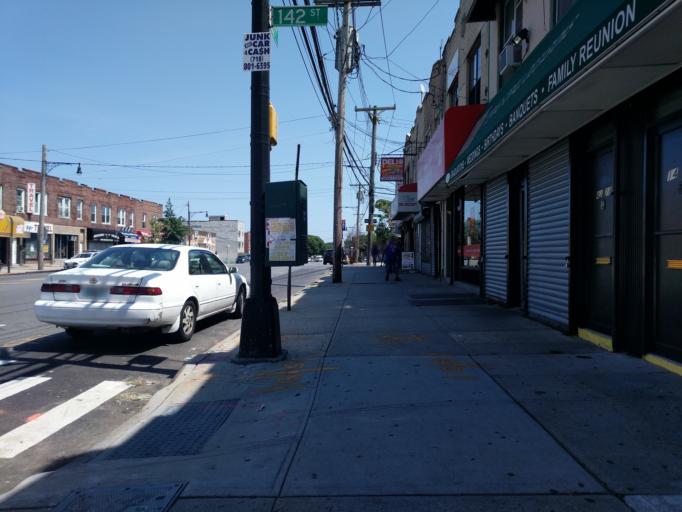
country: US
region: New York
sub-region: Queens County
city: Jamaica
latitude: 40.6740
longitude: -73.7990
